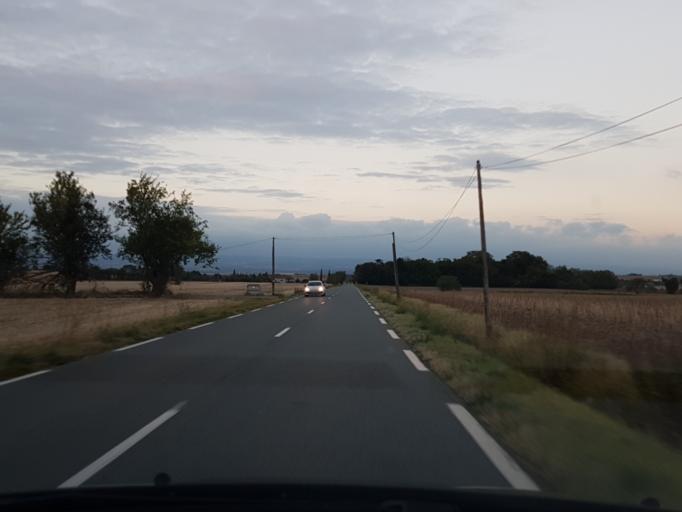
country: FR
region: Languedoc-Roussillon
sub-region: Departement de l'Aude
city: Bram
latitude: 43.2061
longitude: 2.0641
